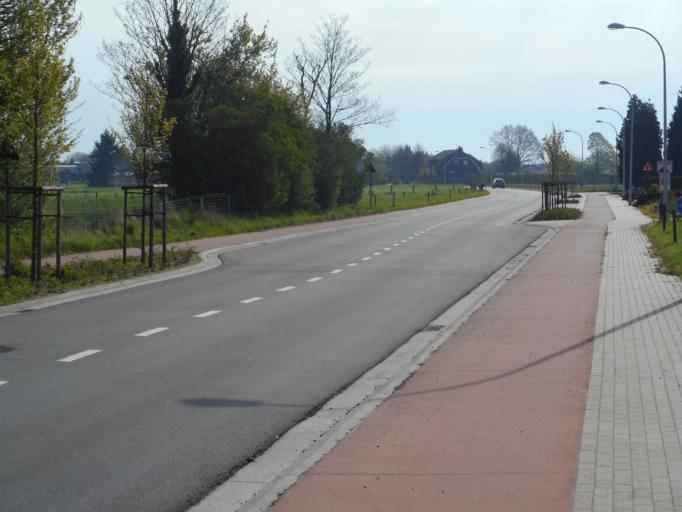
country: BE
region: Flanders
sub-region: Provincie Antwerpen
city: Putte
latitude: 51.0885
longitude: 4.6200
